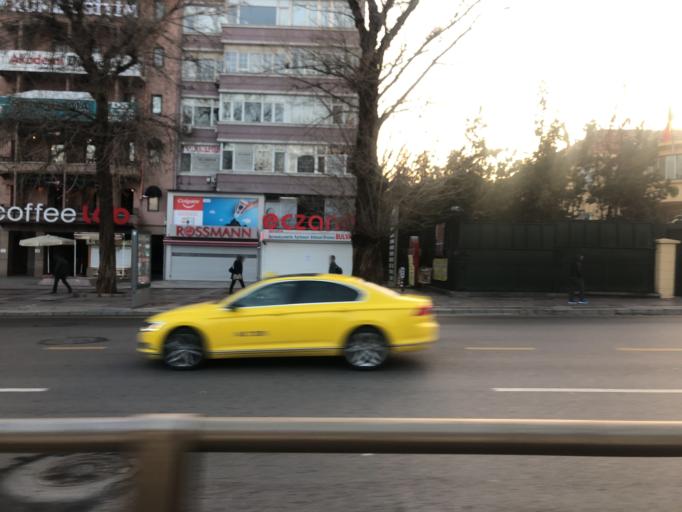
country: TR
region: Ankara
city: Ankara
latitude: 39.9157
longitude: 32.8541
